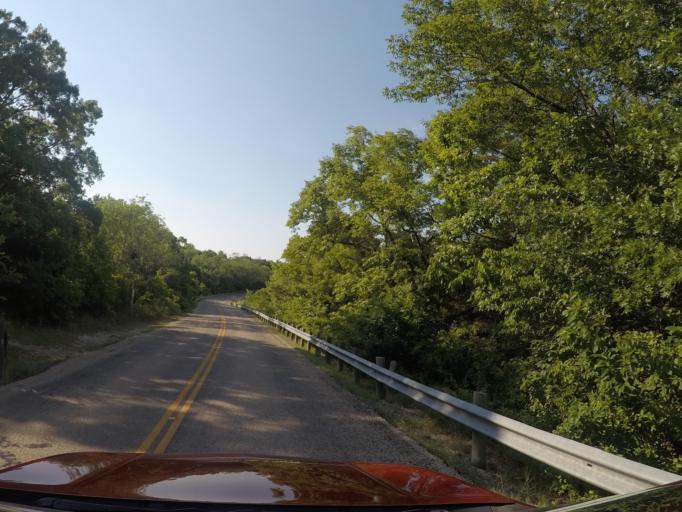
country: US
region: Texas
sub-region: Grayson County
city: Preston
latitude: 33.8122
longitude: -96.6090
